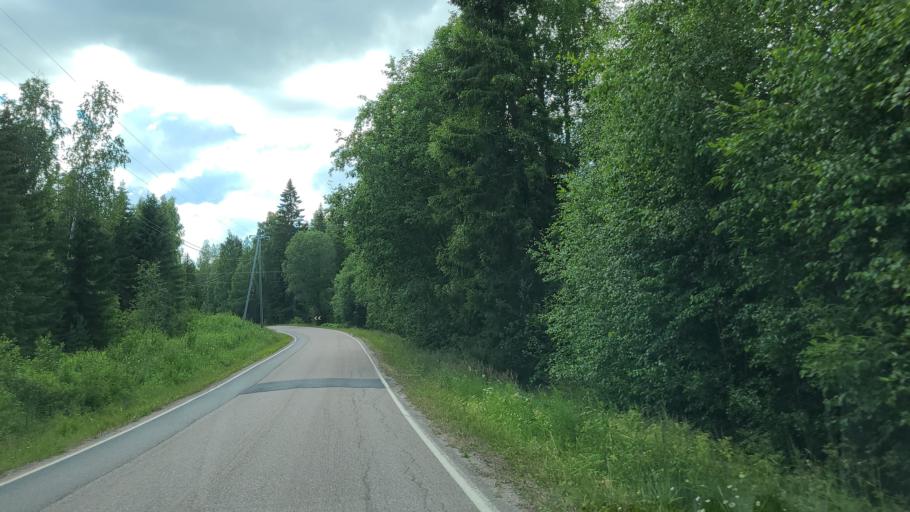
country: FI
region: Central Finland
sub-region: Jaemsae
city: Jaemsae
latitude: 61.9033
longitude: 25.2748
